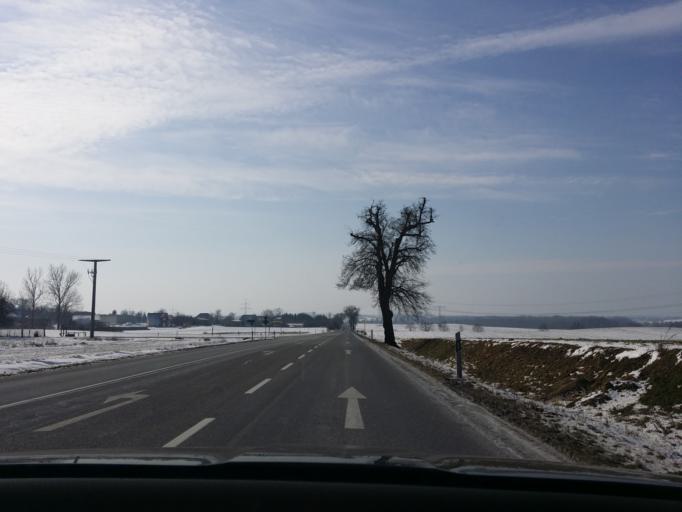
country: DE
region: Mecklenburg-Vorpommern
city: Wulkenzin
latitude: 53.5241
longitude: 13.1307
